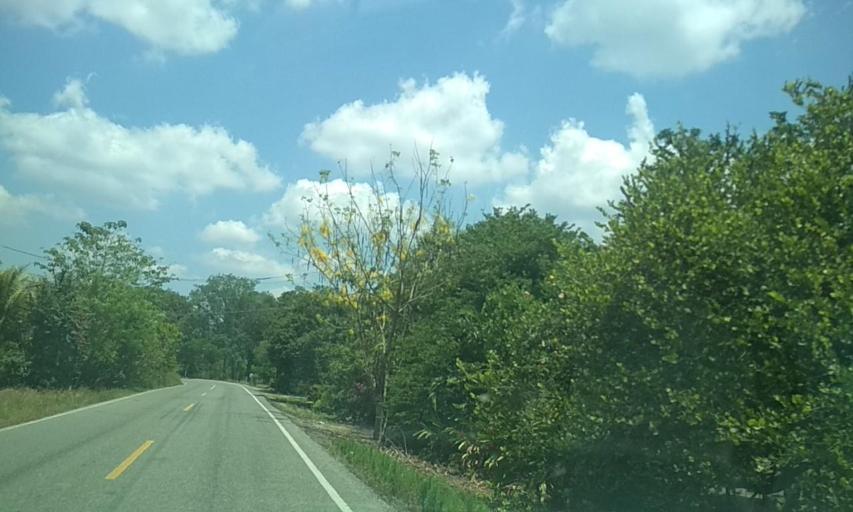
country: MX
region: Tabasco
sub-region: Huimanguillo
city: Huapacal 1ra. Seccion
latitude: 17.7527
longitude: -93.7297
